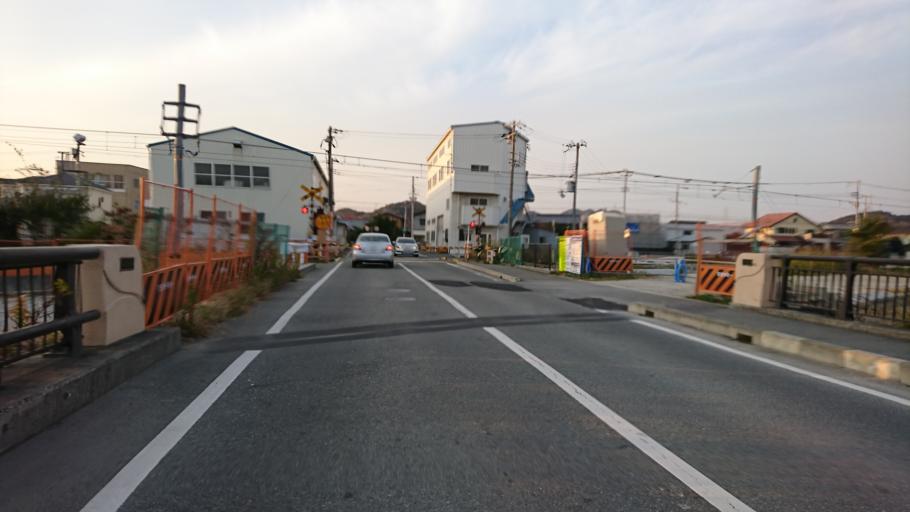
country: JP
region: Hyogo
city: Kakogawacho-honmachi
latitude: 34.7790
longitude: 134.8580
